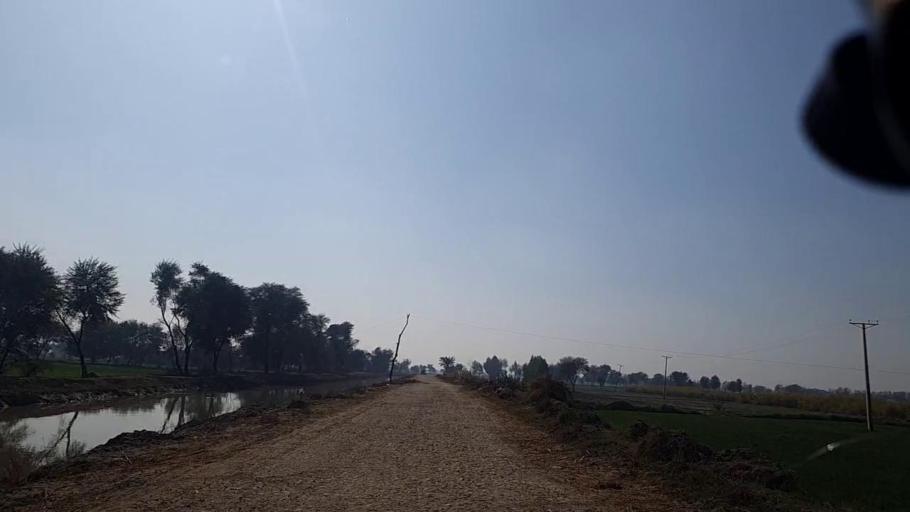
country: PK
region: Sindh
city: Khanpur
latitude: 27.8035
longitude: 69.4118
